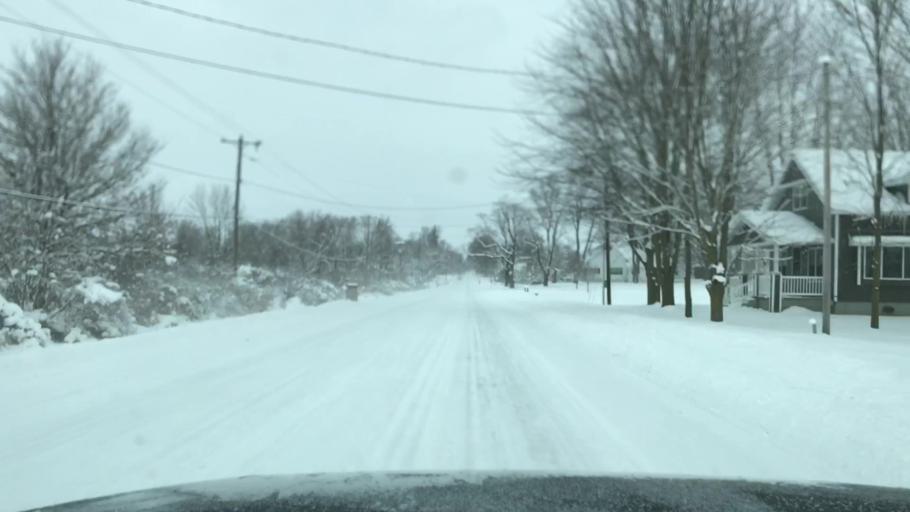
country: US
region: Michigan
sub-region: Ottawa County
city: Hudsonville
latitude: 42.8203
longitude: -85.8422
